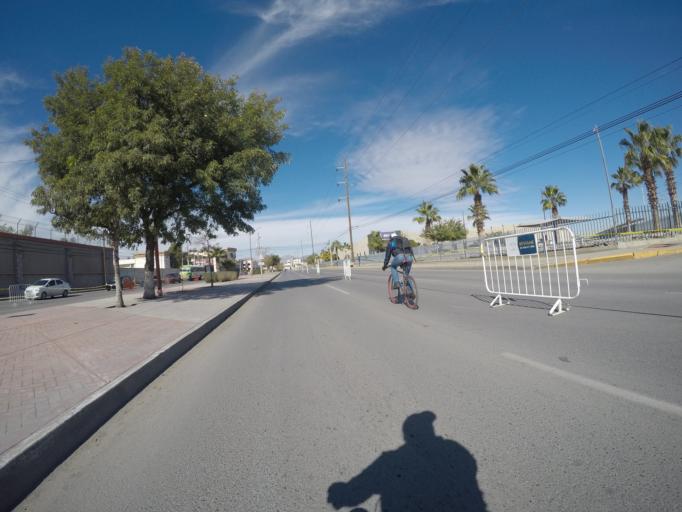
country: MX
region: Chihuahua
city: Ciudad Juarez
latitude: 31.7199
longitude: -106.3979
